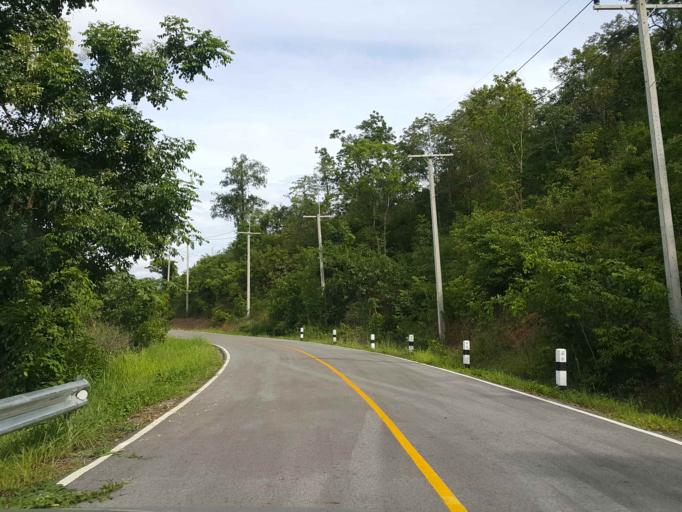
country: TH
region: Sukhothai
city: Thung Saliam
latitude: 17.2410
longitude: 99.4952
